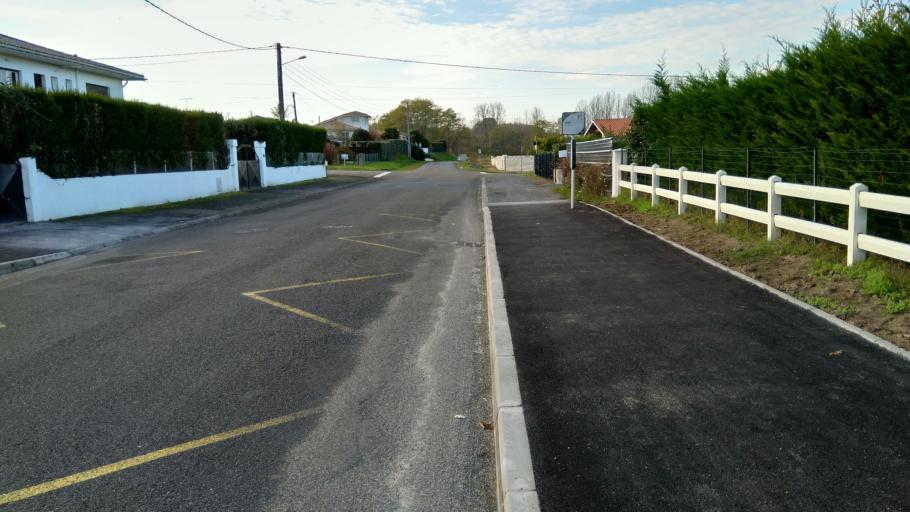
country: FR
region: Aquitaine
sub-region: Departement des Landes
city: Saint-Paul-les-Dax
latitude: 43.7345
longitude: -1.0622
